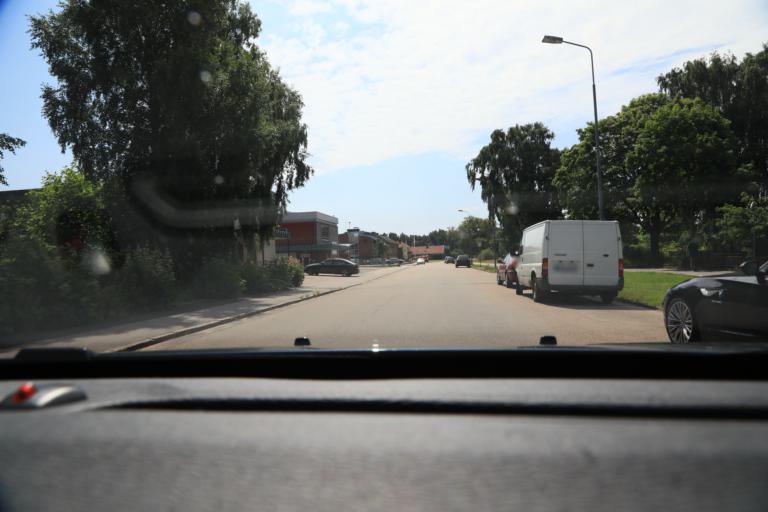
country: SE
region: Halland
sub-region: Halmstads Kommun
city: Halmstad
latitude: 56.6655
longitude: 12.8537
